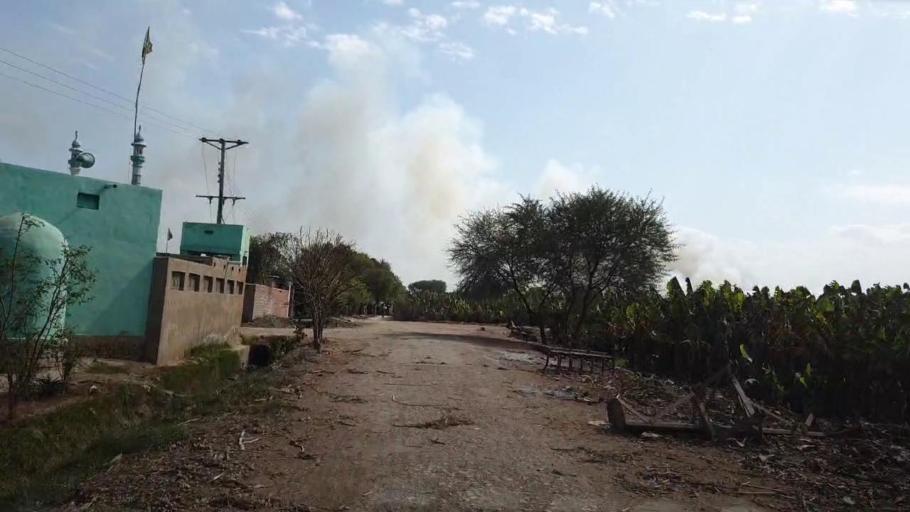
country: PK
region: Sindh
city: Matiari
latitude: 25.5537
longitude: 68.5593
